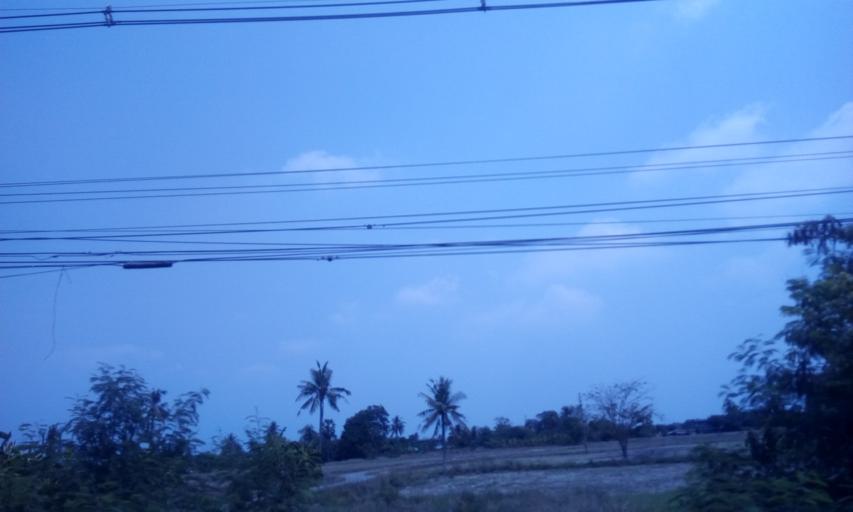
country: TH
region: Chachoengsao
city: Chachoengsao
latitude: 13.7408
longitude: 101.0841
